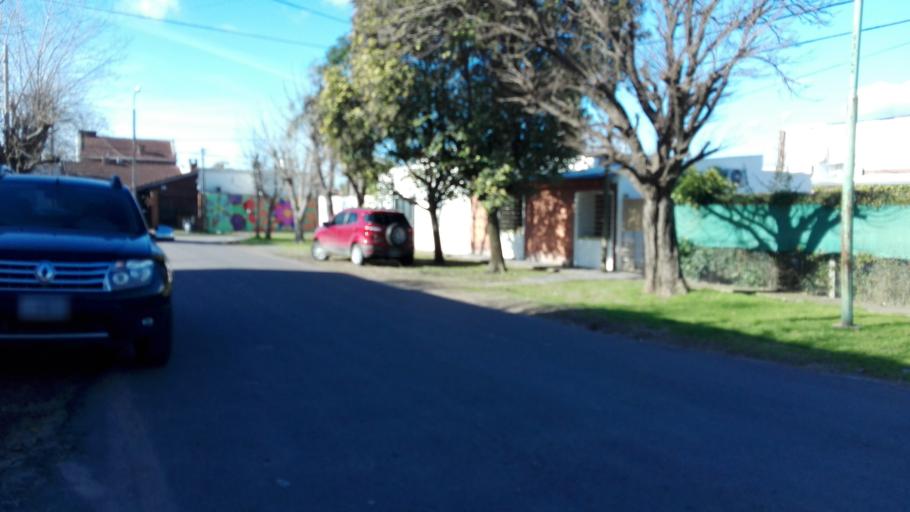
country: AR
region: Buenos Aires
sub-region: Partido de La Plata
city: La Plata
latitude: -34.8874
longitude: -57.9958
